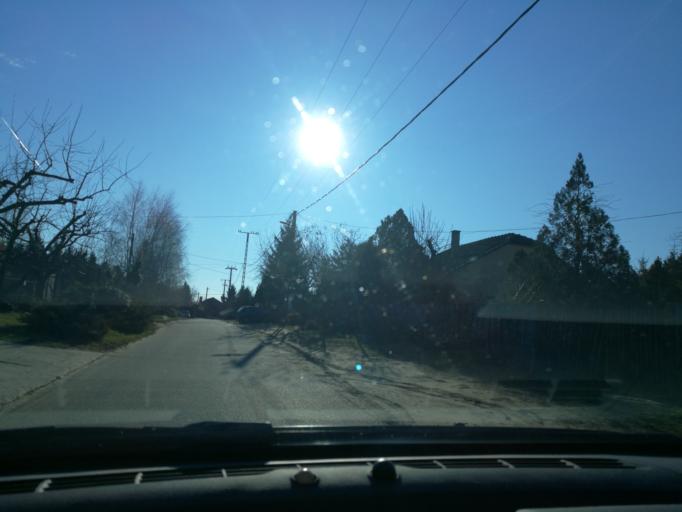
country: HU
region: Szabolcs-Szatmar-Bereg
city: Nyiregyhaza
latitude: 47.9476
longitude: 21.7515
